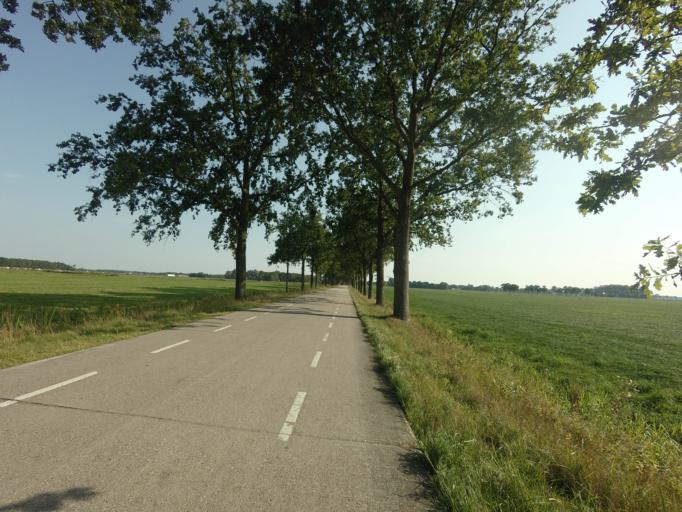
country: NL
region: Groningen
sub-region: Gemeente Zuidhorn
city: Aduard
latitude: 53.1796
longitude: 6.4736
